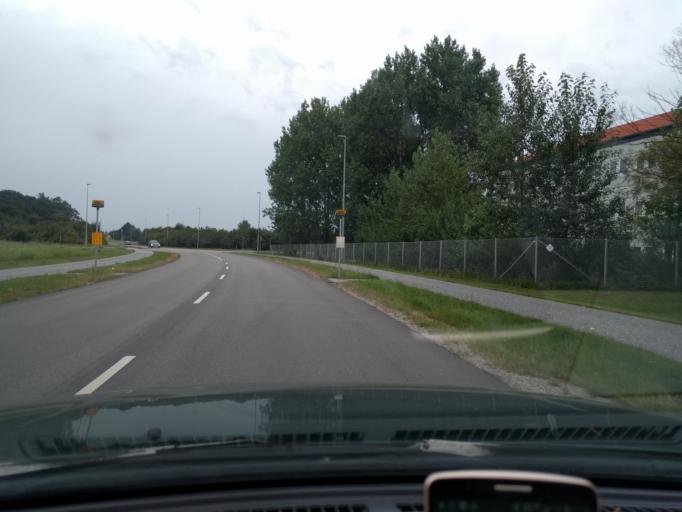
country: DK
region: Zealand
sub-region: Slagelse Kommune
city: Korsor
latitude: 55.3511
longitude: 11.1274
